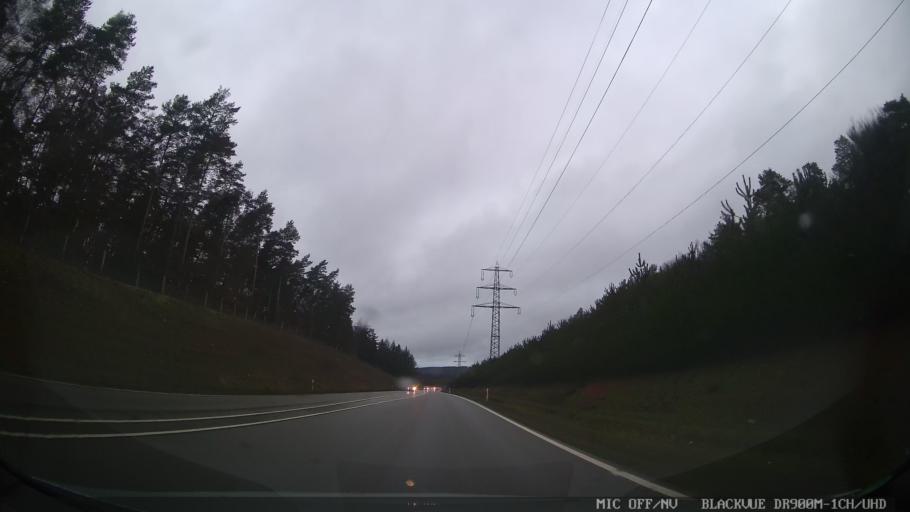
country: DE
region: Saarland
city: Mettlach
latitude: 49.4827
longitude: 6.6174
